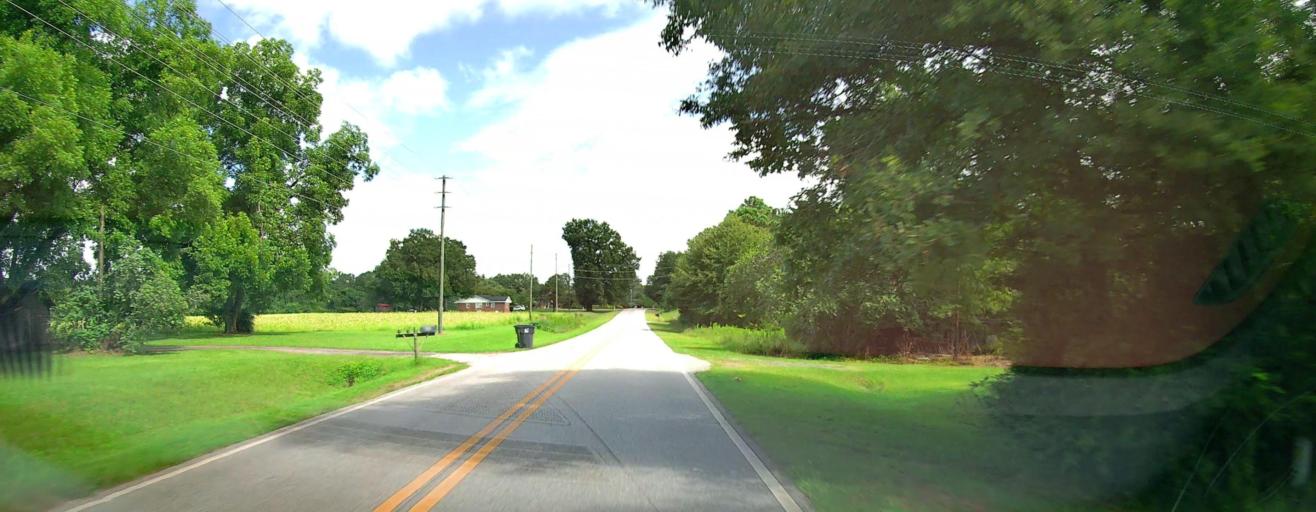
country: US
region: Georgia
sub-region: Peach County
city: Byron
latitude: 32.6136
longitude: -83.7968
